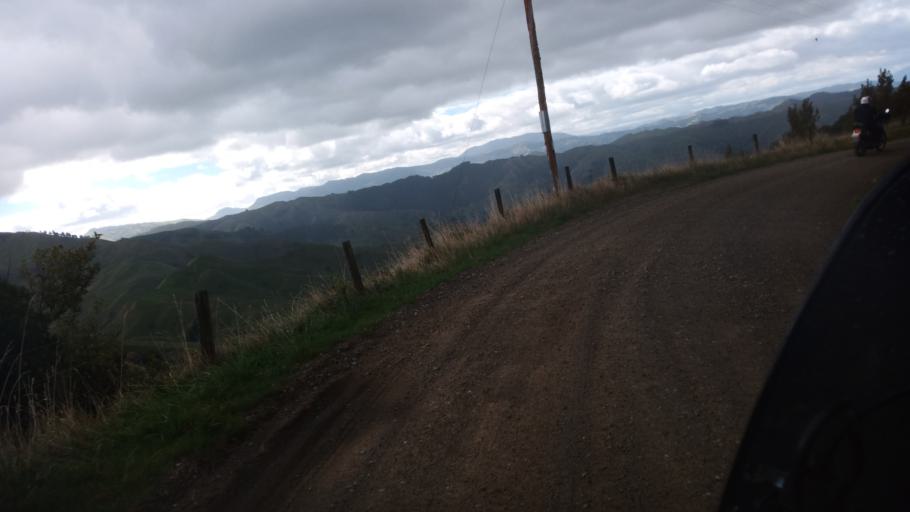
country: NZ
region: Gisborne
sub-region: Gisborne District
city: Gisborne
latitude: -38.4772
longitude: 177.6115
